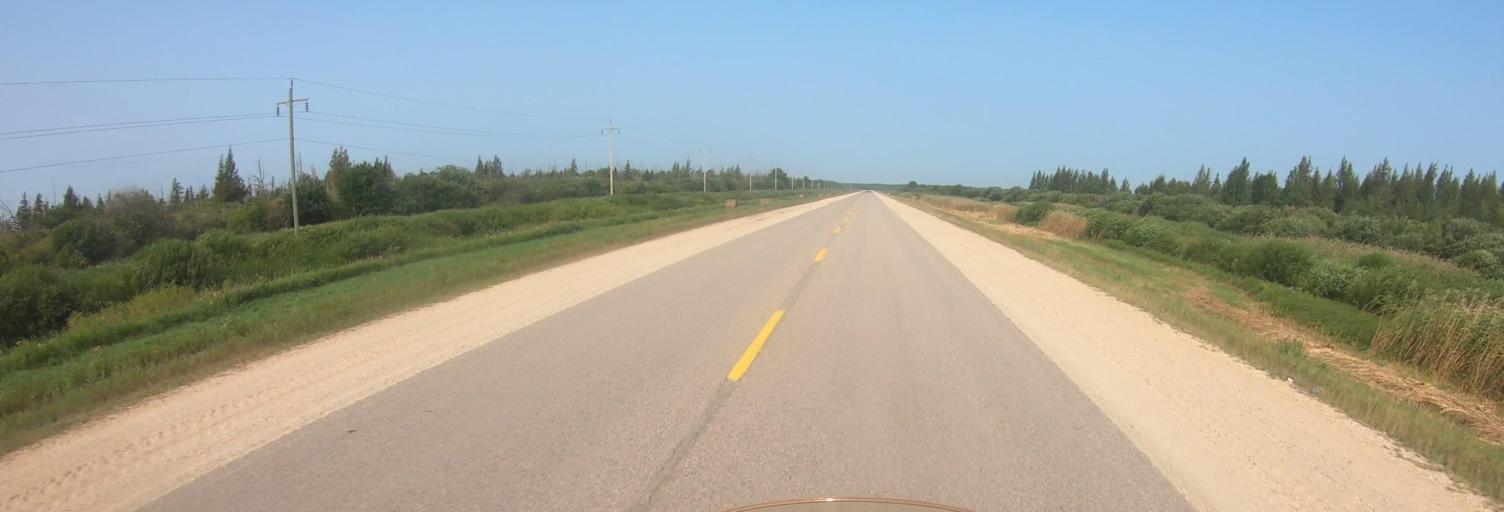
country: US
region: Minnesota
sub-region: Roseau County
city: Warroad
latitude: 49.0170
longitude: -95.5410
